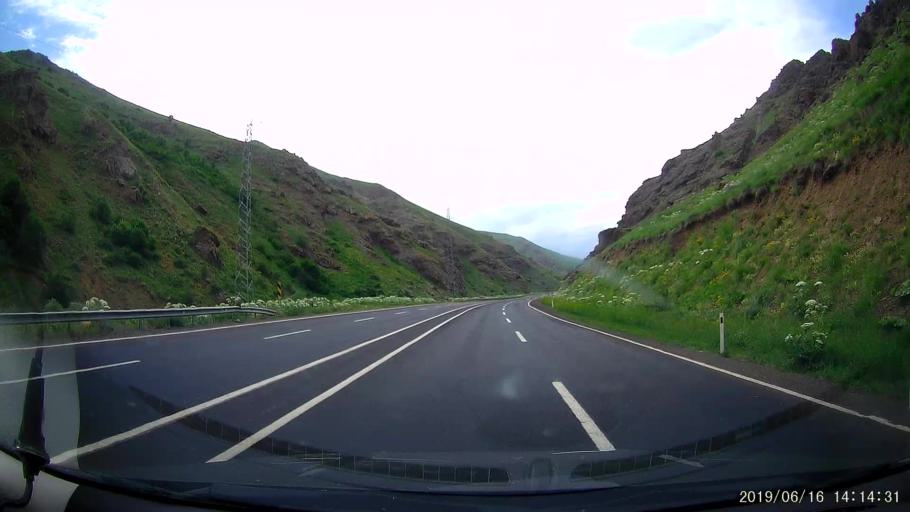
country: TR
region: Agri
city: Tahir
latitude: 39.7959
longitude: 42.4961
